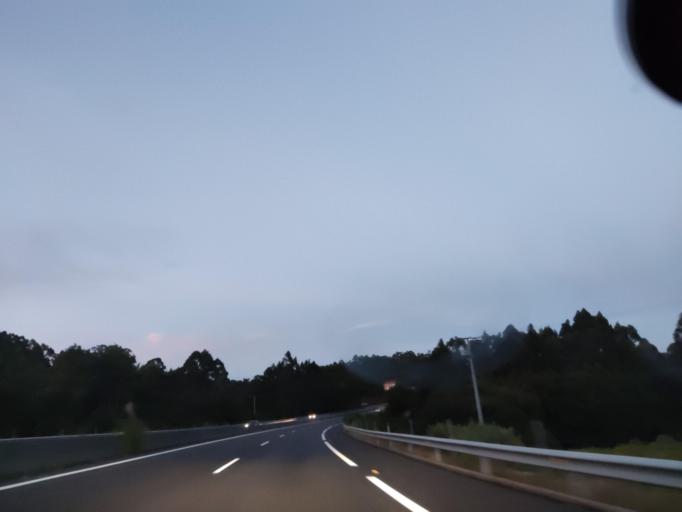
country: ES
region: Galicia
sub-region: Provincia da Coruna
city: Boiro
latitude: 42.6229
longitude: -8.9439
